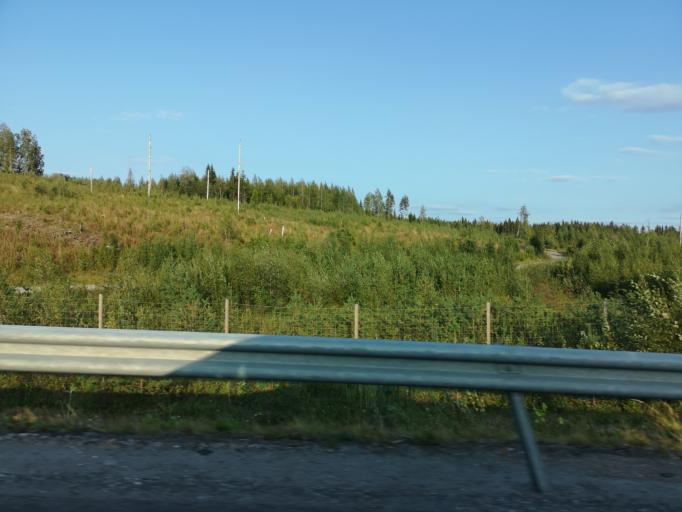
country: FI
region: Paijanne Tavastia
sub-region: Lahti
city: Heinola
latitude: 61.3603
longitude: 26.0425
